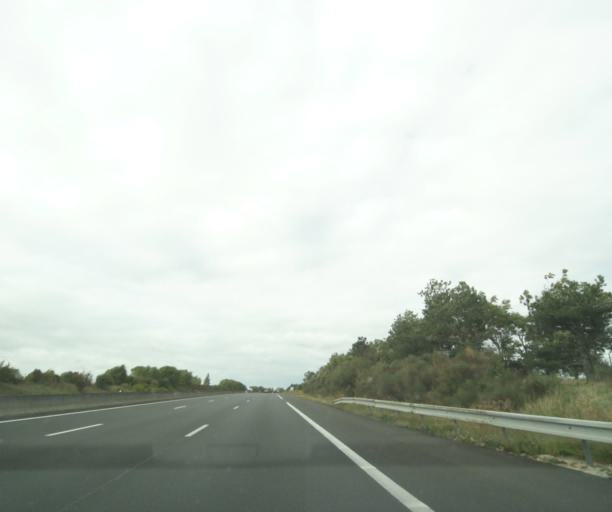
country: FR
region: Centre
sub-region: Departement d'Eure-et-Loir
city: Janville
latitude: 48.2560
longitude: 1.8517
